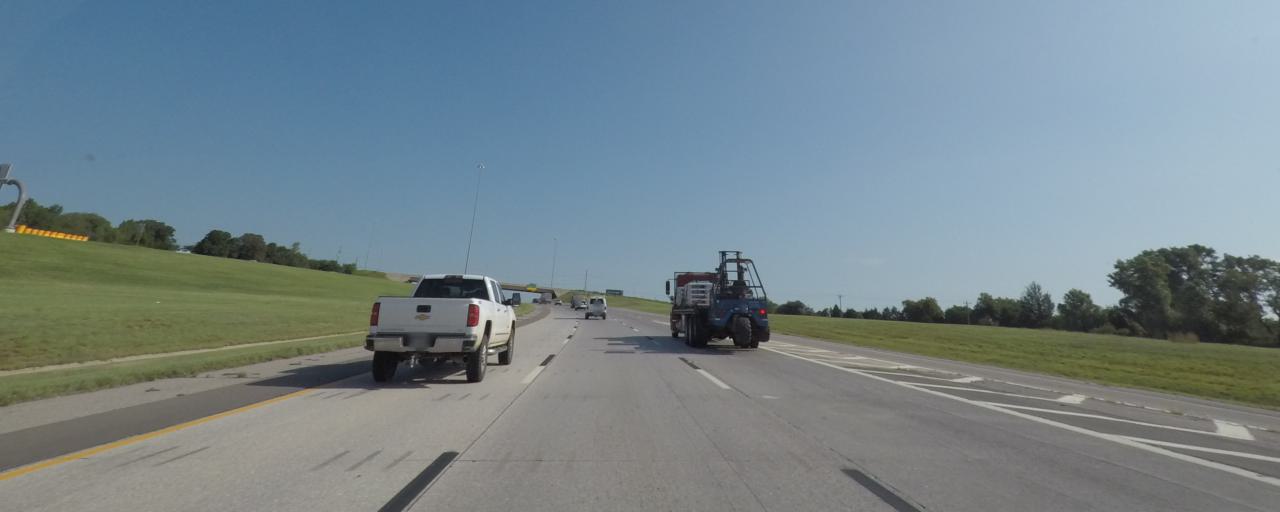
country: US
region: Oklahoma
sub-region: Oklahoma County
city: Edmond
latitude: 35.6058
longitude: -97.4259
